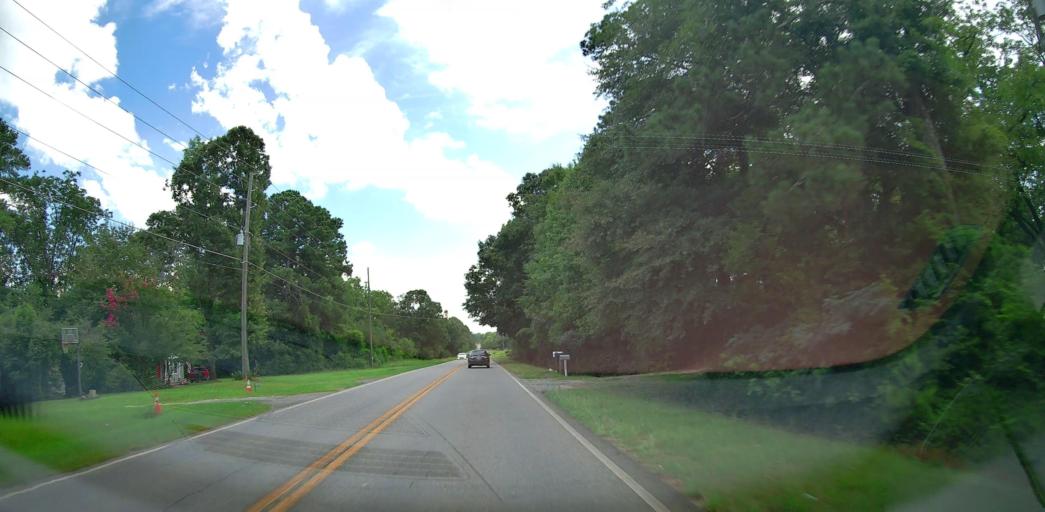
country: US
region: Georgia
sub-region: Houston County
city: Perry
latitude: 32.5431
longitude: -83.7200
